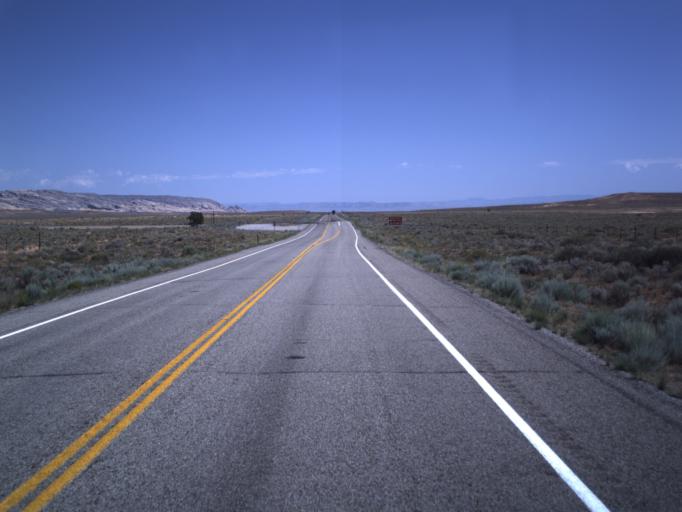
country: US
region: Utah
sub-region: Emery County
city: Ferron
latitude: 38.6279
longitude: -110.5683
